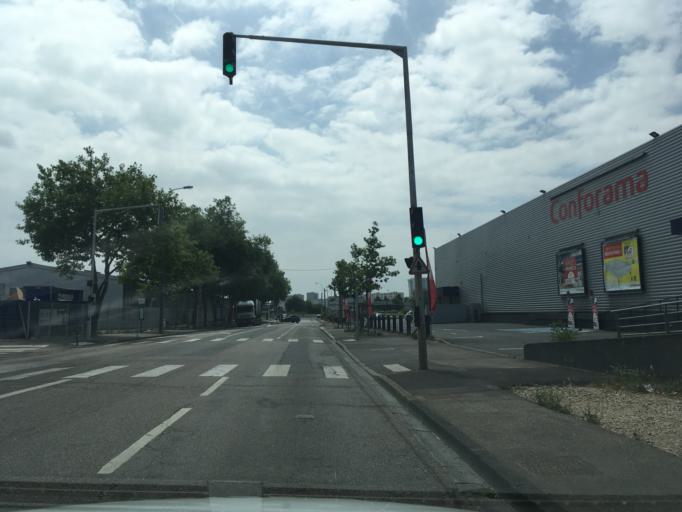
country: FR
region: Lorraine
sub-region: Departement de Meurthe-et-Moselle
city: Tomblaine
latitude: 48.6796
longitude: 6.2045
